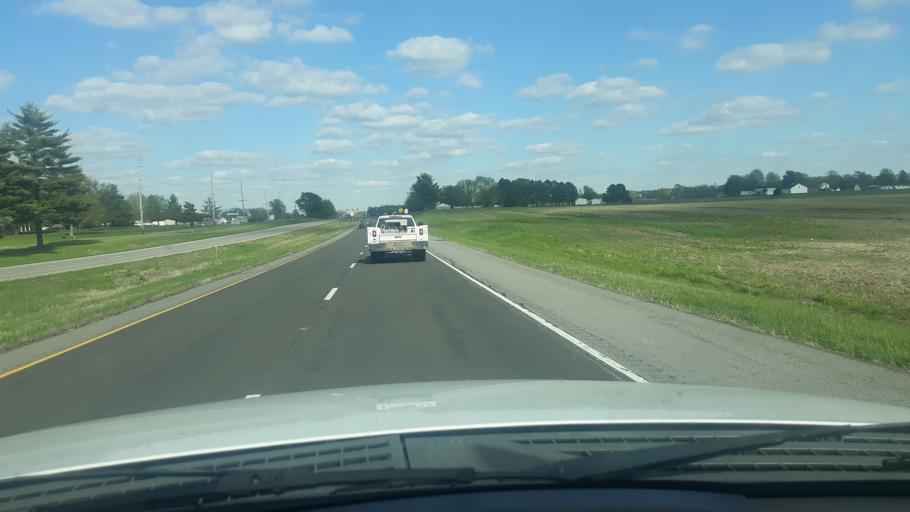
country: US
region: Illinois
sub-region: Williamson County
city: Marion
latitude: 37.7300
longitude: -88.8606
